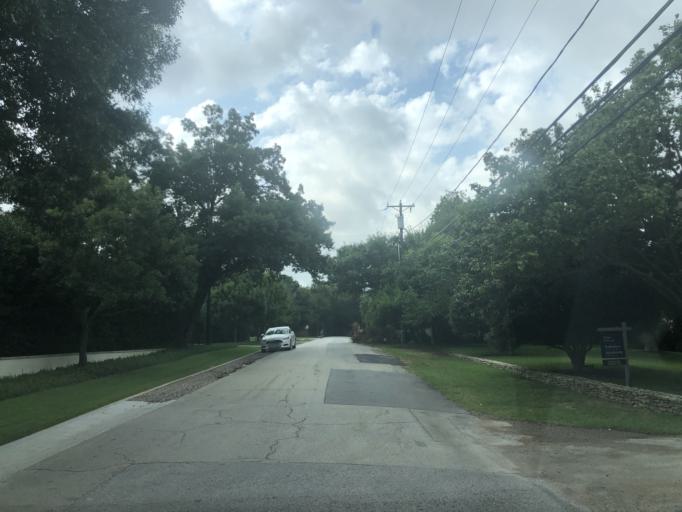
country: US
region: Texas
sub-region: Dallas County
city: University Park
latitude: 32.8610
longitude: -96.8266
